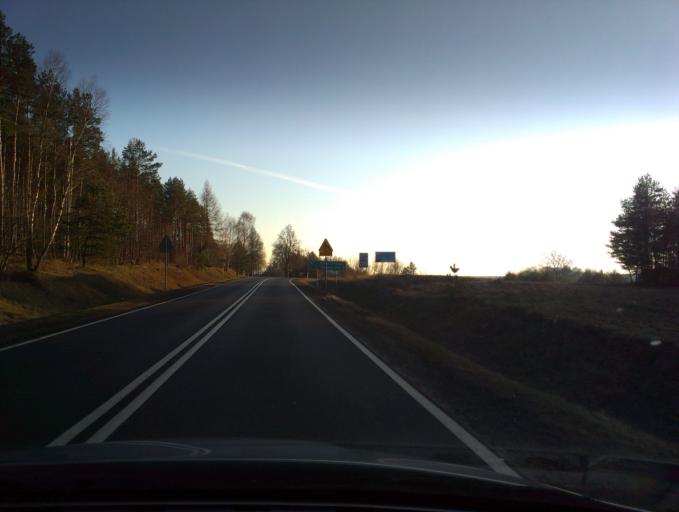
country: PL
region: West Pomeranian Voivodeship
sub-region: Powiat szczecinecki
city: Borne Sulinowo
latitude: 53.6084
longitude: 16.5824
